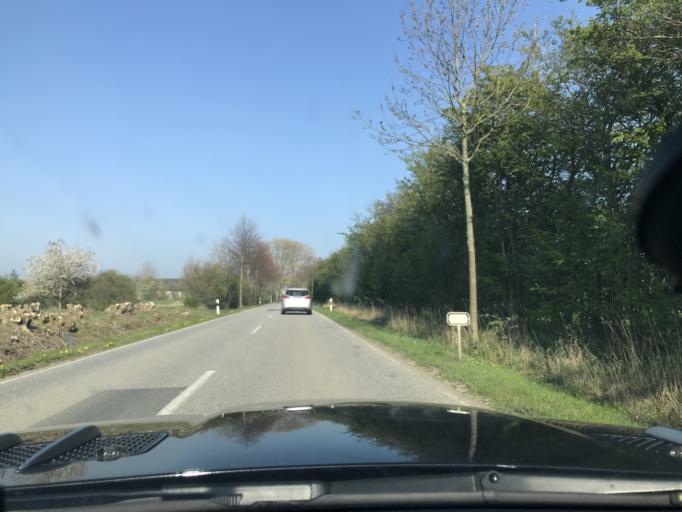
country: DE
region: Schleswig-Holstein
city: Grossenbrode
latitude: 54.3638
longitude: 11.0568
